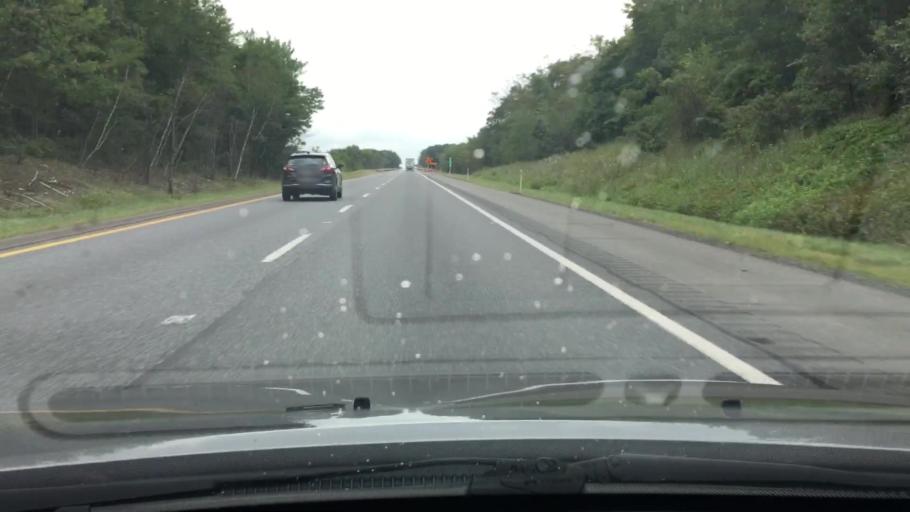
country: US
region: Pennsylvania
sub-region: Schuylkill County
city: Tremont
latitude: 40.6881
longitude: -76.3757
